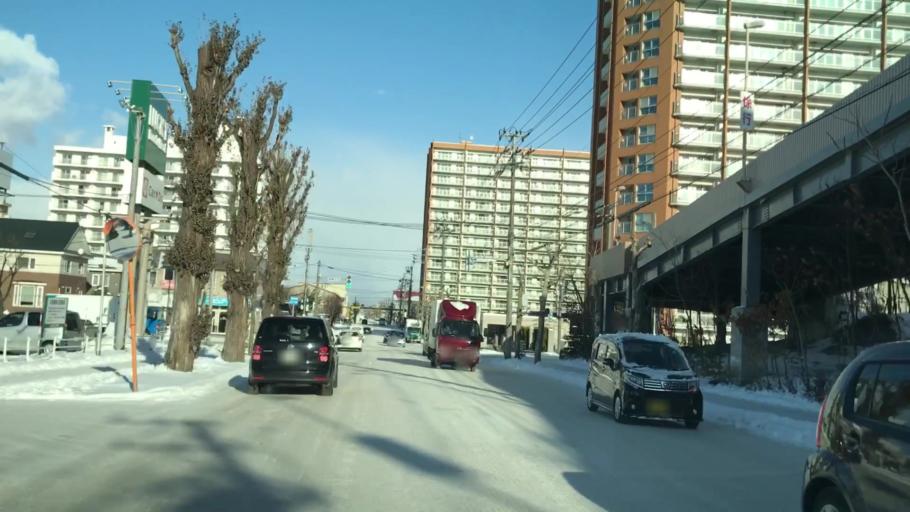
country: JP
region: Hokkaido
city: Sapporo
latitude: 43.0973
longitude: 141.2762
